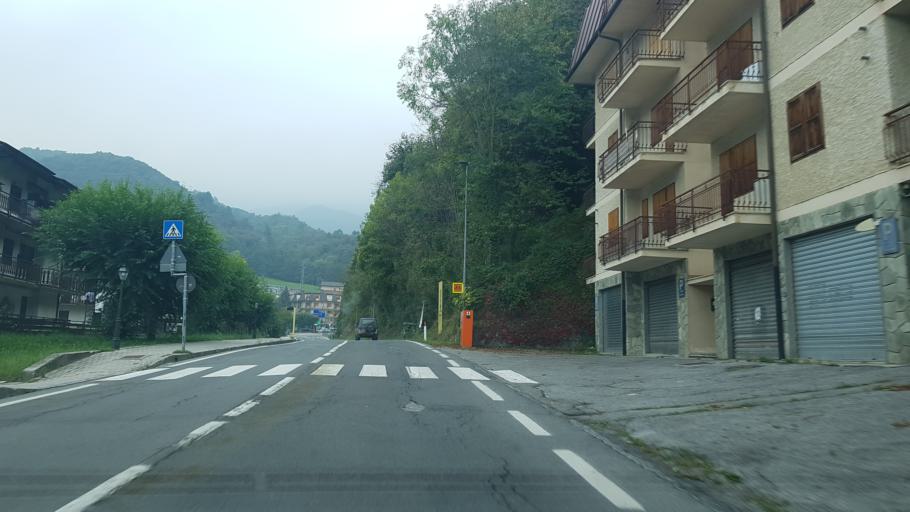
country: IT
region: Piedmont
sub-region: Provincia di Cuneo
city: Frabosa Sottana
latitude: 44.3054
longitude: 7.8006
